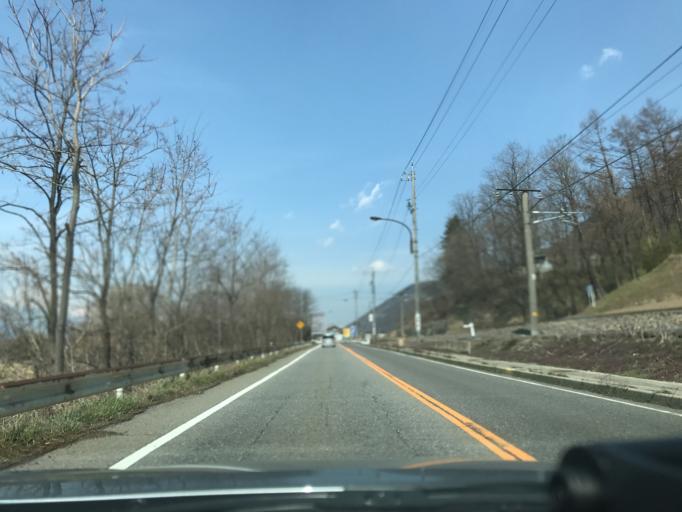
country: JP
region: Nagano
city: Toyoshina
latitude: 36.2909
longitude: 137.9439
